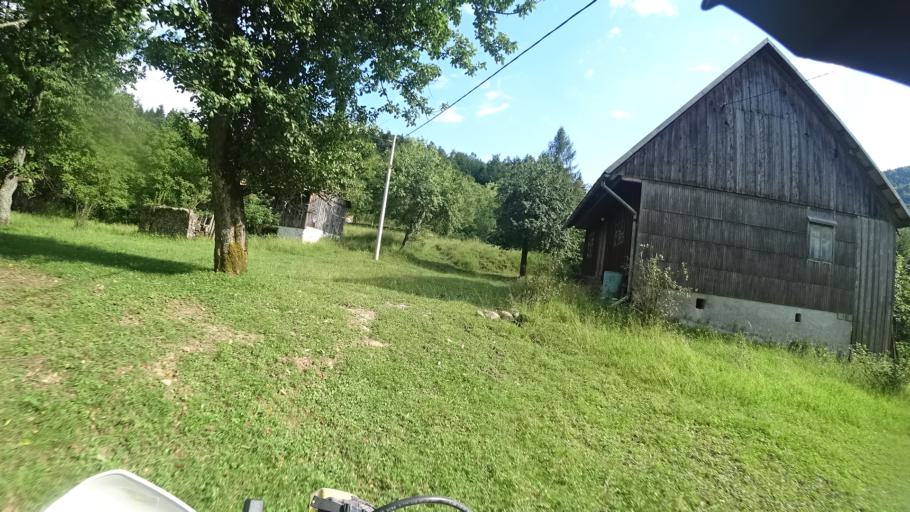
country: SI
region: Osilnica
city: Osilnica
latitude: 45.4737
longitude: 14.6999
